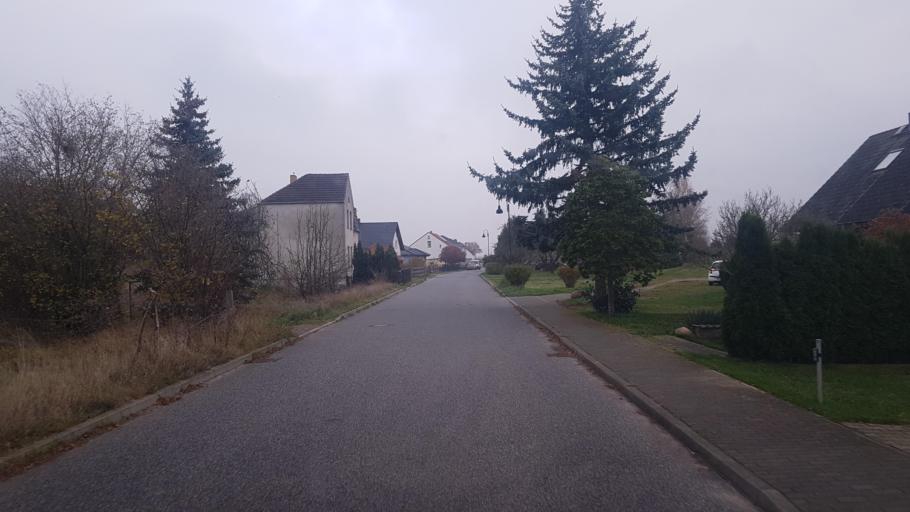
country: DE
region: Brandenburg
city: Gross Kreutz
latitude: 52.3995
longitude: 12.7792
